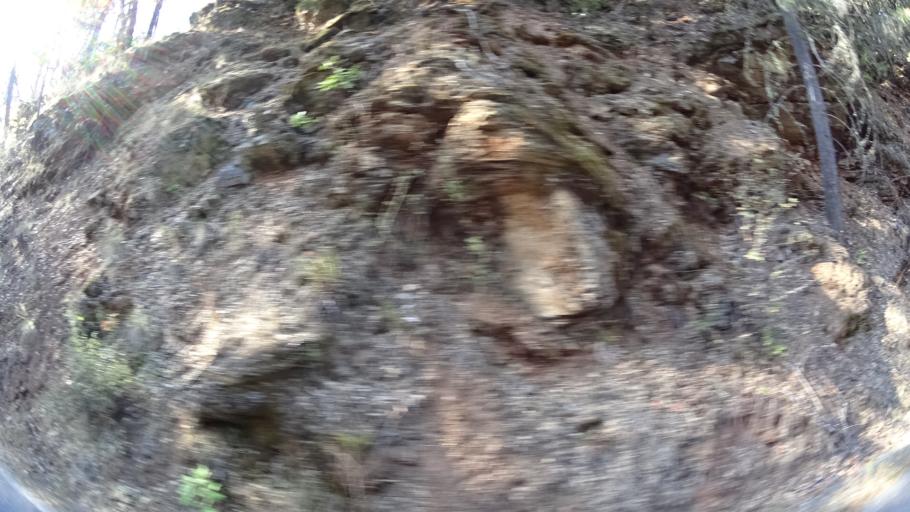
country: US
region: California
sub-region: Siskiyou County
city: Happy Camp
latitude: 41.7608
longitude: -123.0151
